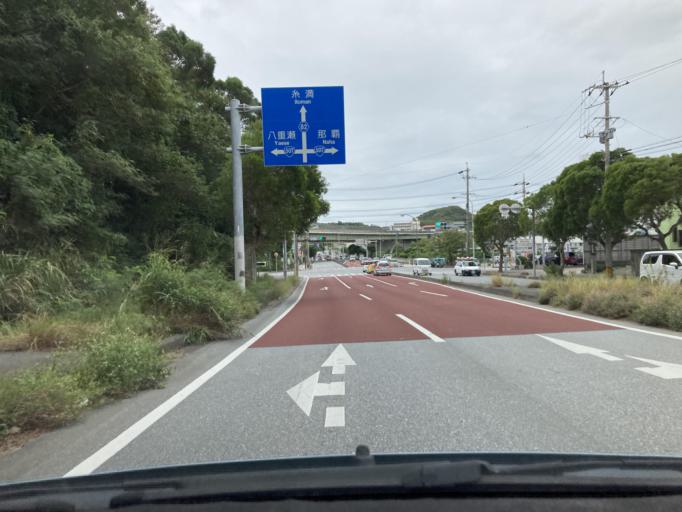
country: JP
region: Okinawa
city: Tomigusuku
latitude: 26.1811
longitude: 127.7169
